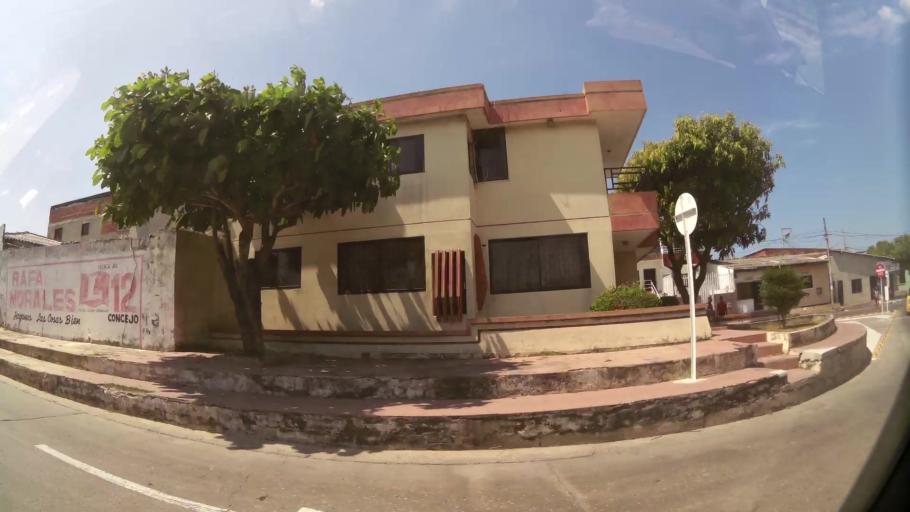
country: CO
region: Atlantico
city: Barranquilla
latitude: 10.9618
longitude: -74.8033
